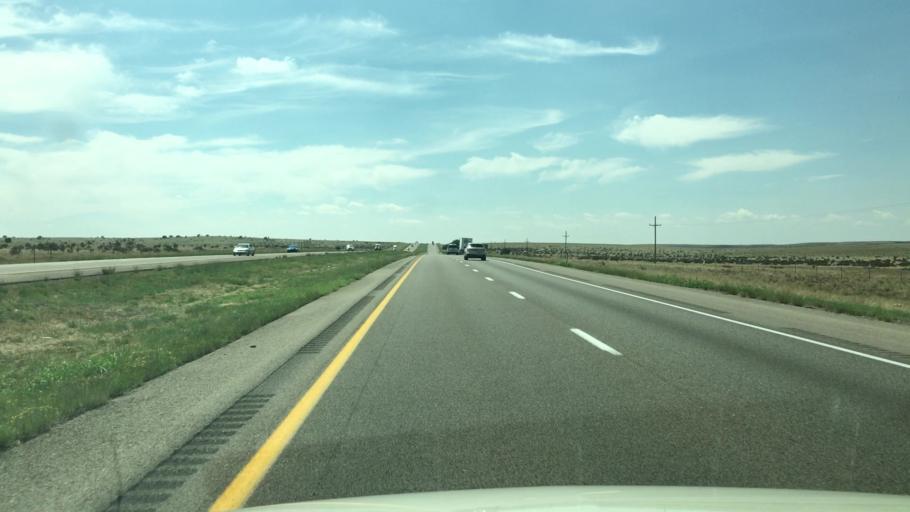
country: US
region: New Mexico
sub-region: Guadalupe County
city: Santa Rosa
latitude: 34.9787
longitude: -105.0331
